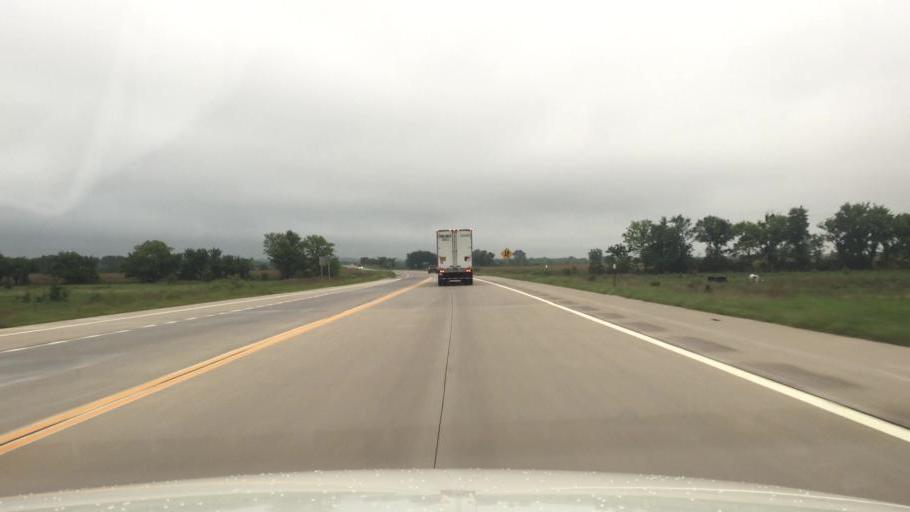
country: US
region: Kansas
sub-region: Montgomery County
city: Cherryvale
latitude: 37.2073
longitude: -95.5849
